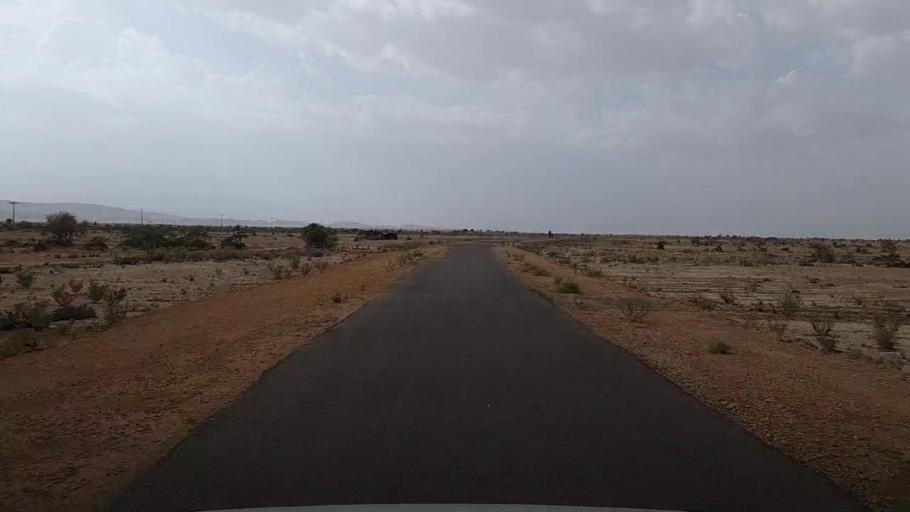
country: PK
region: Sindh
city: Jamshoro
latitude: 25.4490
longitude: 67.6789
